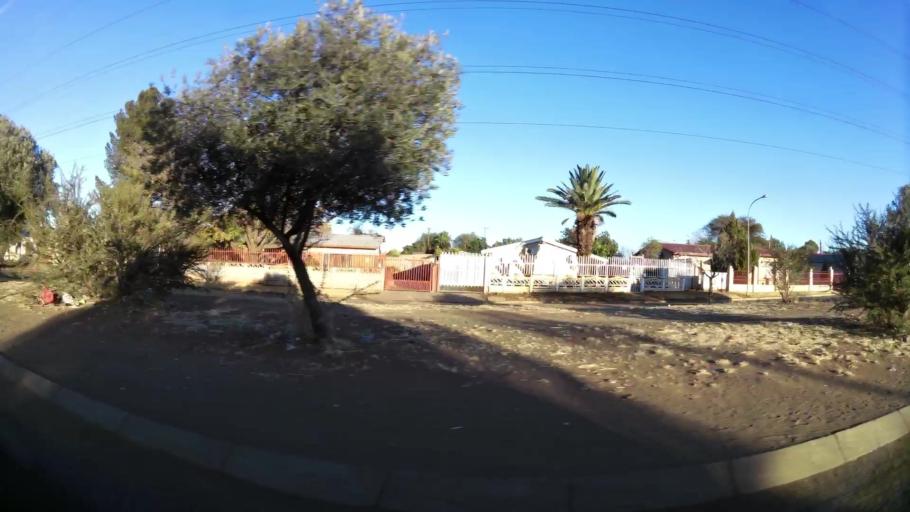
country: ZA
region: Northern Cape
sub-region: Frances Baard District Municipality
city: Kimberley
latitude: -28.7709
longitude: 24.7645
